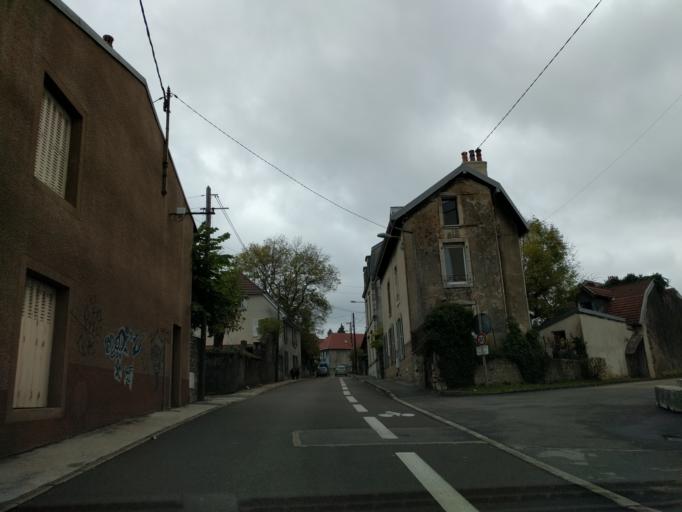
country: FR
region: Franche-Comte
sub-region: Departement du Doubs
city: Besancon
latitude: 47.2508
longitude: 6.0268
